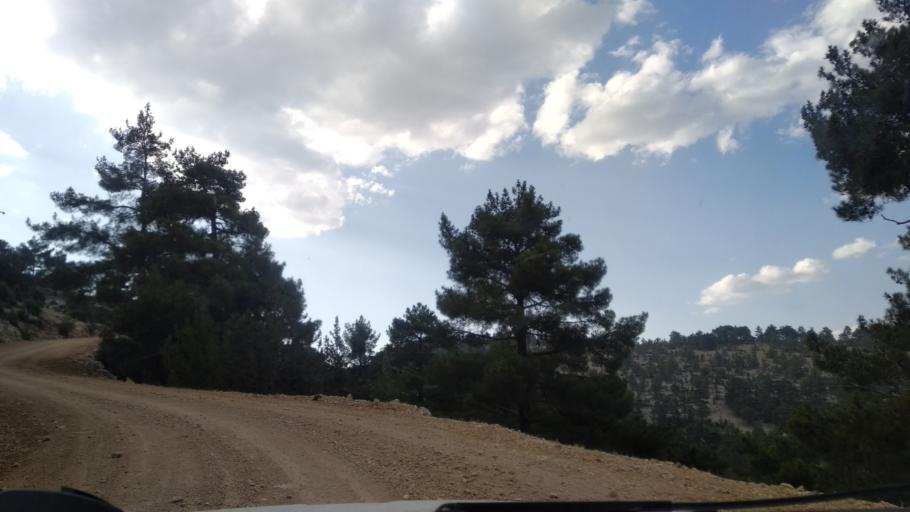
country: TR
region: Mersin
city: Sarikavak
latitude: 36.5984
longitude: 33.7043
